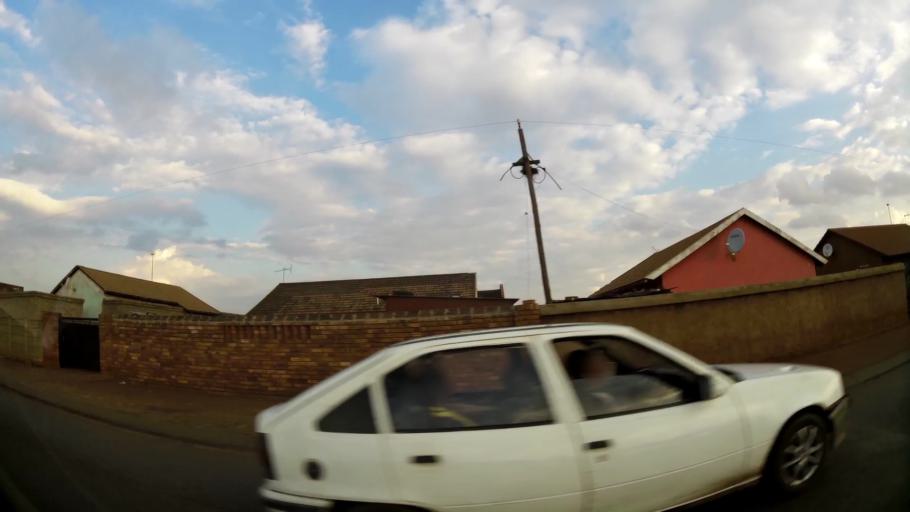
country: ZA
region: Gauteng
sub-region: City of Johannesburg Metropolitan Municipality
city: Orange Farm
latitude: -26.5936
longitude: 27.8353
